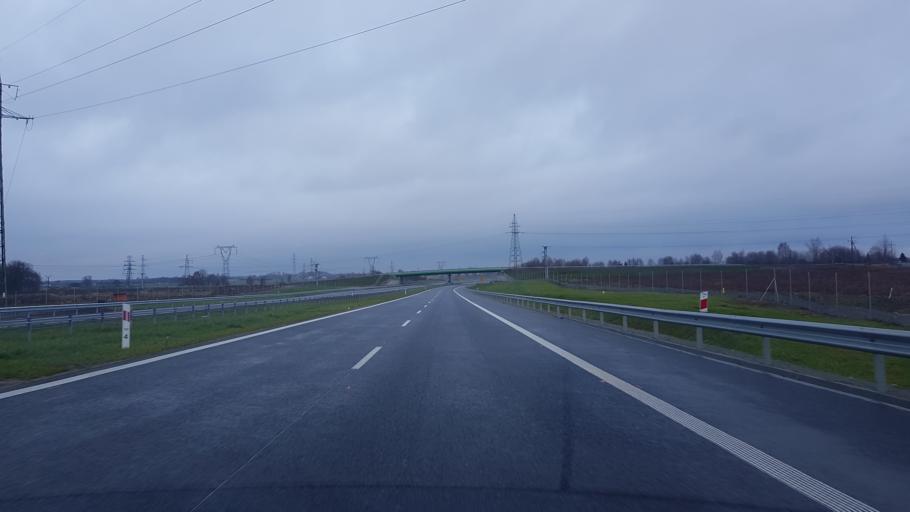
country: PL
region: West Pomeranian Voivodeship
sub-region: Koszalin
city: Koszalin
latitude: 54.2204
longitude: 16.1610
